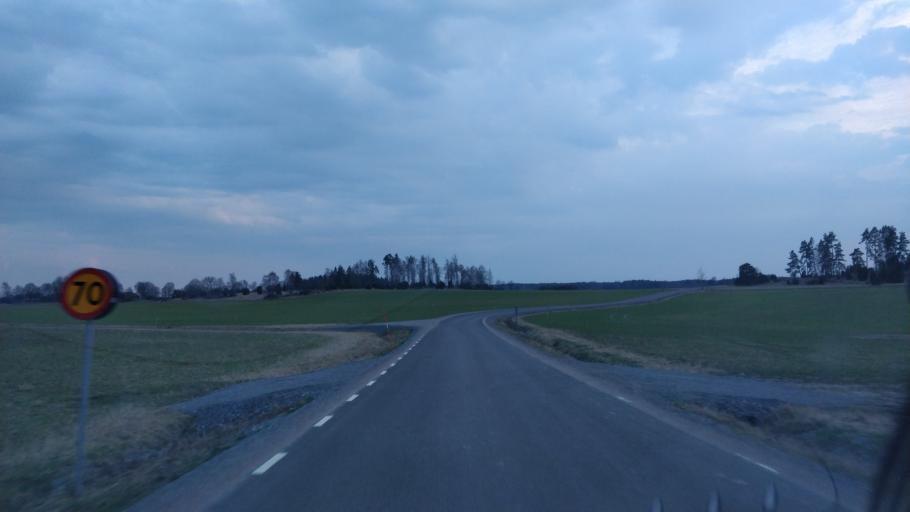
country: SE
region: Uppsala
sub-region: Enkopings Kommun
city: Orsundsbro
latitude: 59.7215
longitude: 17.2668
